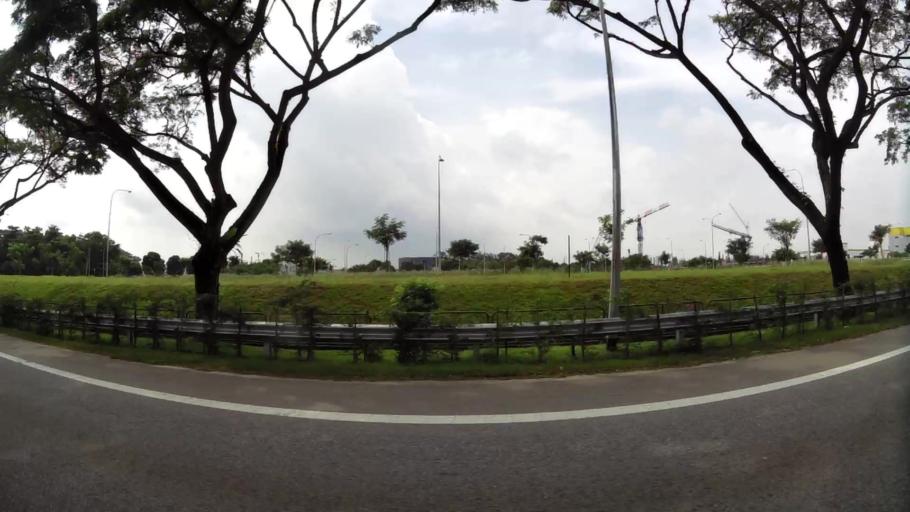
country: MY
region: Johor
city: Kampung Pasir Gudang Baru
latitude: 1.3734
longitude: 103.9366
